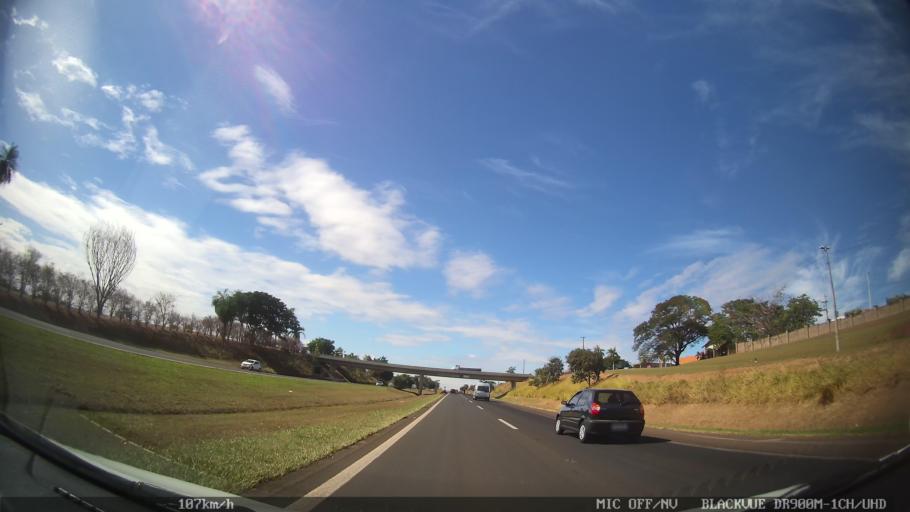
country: BR
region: Sao Paulo
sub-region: Sao Jose Do Rio Preto
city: Sao Jose do Rio Preto
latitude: -20.8160
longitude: -49.4498
